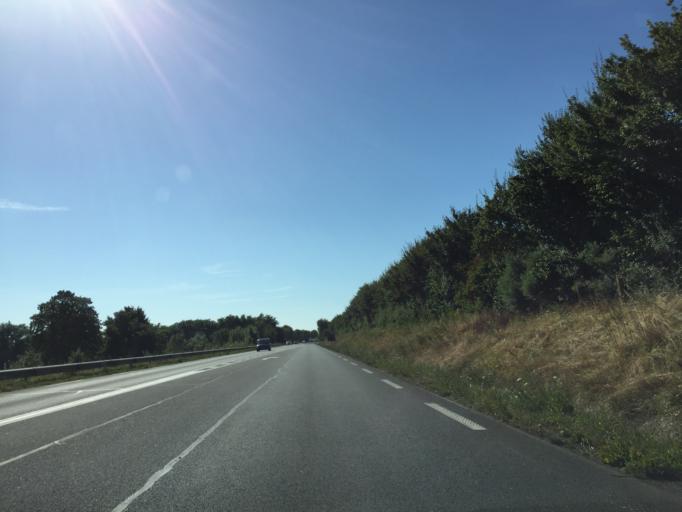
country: FR
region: Lower Normandy
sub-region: Departement du Calvados
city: Lisieux
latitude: 49.1557
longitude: 0.2413
